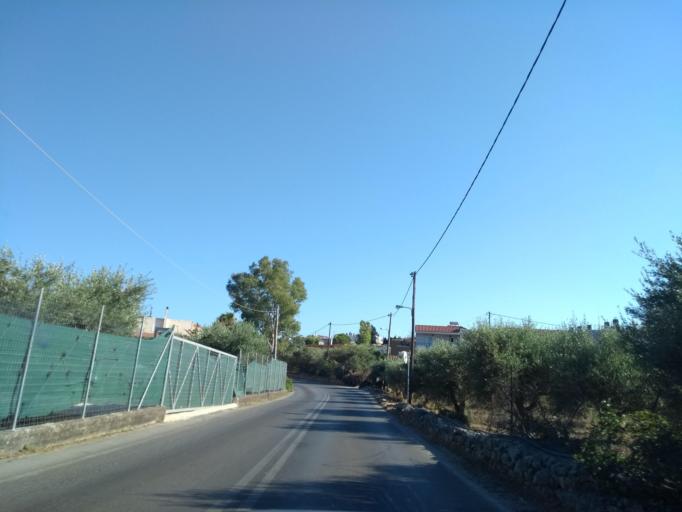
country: GR
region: Crete
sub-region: Nomos Chanias
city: Pithari
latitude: 35.5380
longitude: 24.0814
